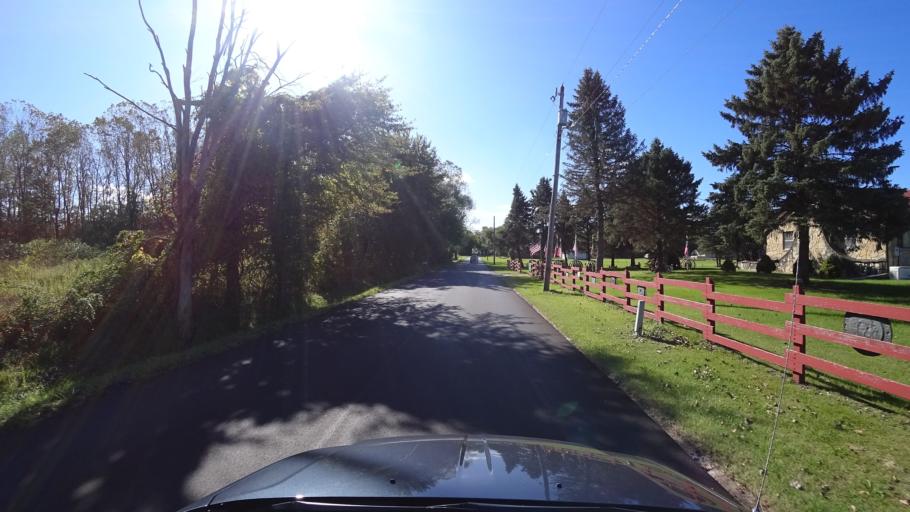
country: US
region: Indiana
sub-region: LaPorte County
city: Michigan City
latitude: 41.6933
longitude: -86.9131
